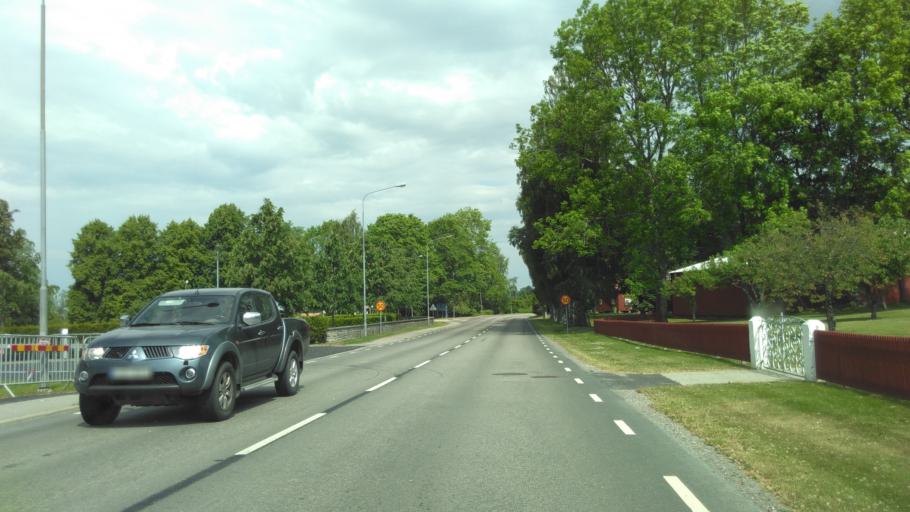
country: SE
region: Vaestra Goetaland
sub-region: Vara Kommun
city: Kvanum
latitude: 58.3809
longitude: 13.1475
